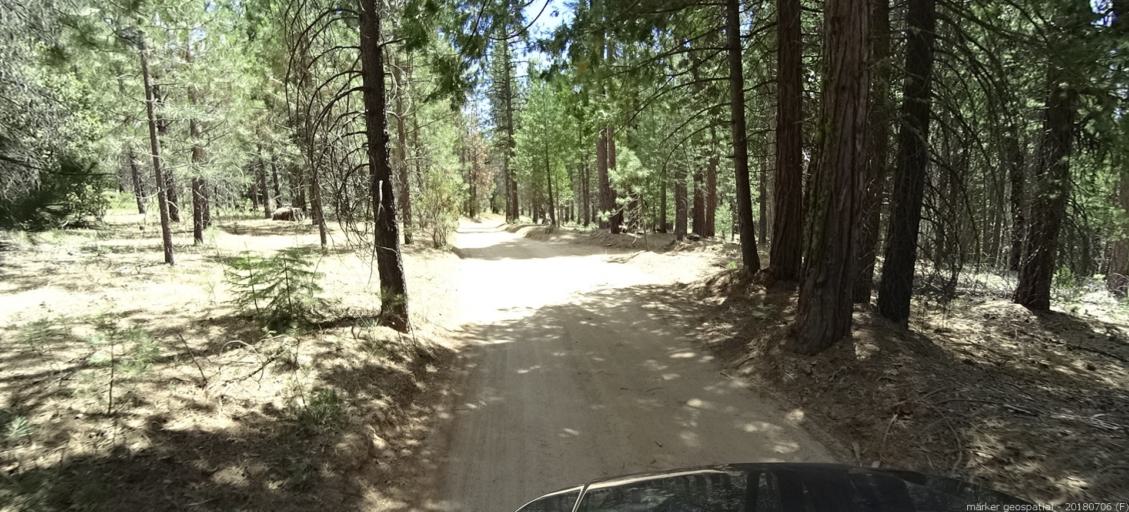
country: US
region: California
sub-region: Madera County
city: Oakhurst
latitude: 37.4158
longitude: -119.3764
